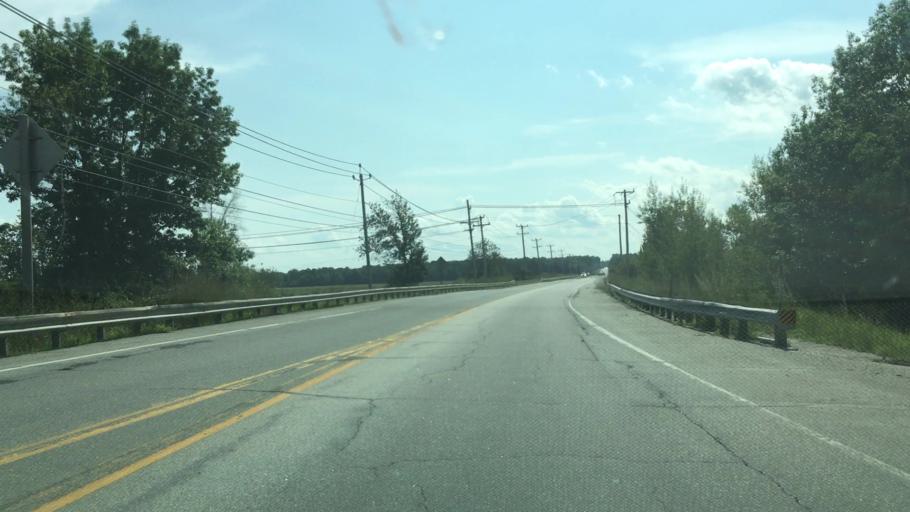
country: US
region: Maine
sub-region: Penobscot County
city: Bangor
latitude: 44.7784
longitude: -68.7979
